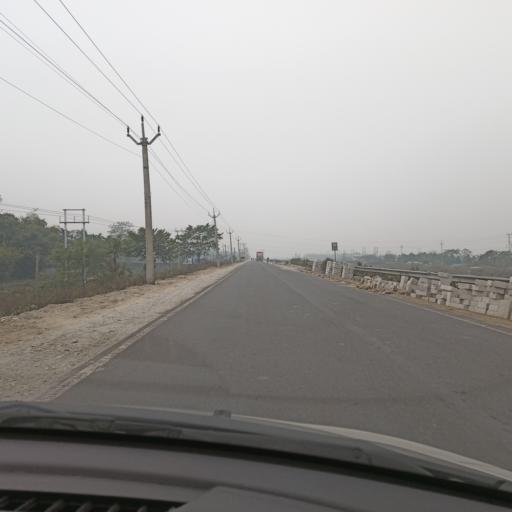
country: IN
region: West Bengal
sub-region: Darjiling
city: Shiliguri
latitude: 26.6610
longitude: 88.4638
